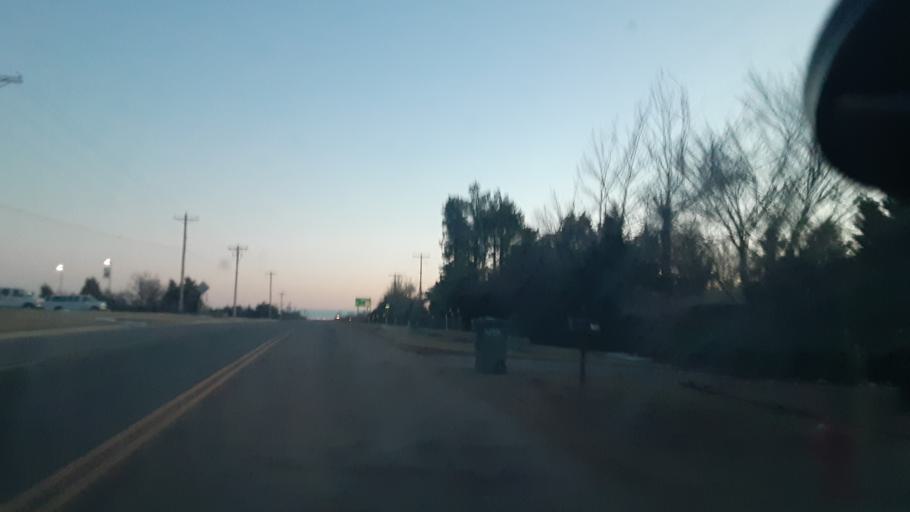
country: US
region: Oklahoma
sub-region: Oklahoma County
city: Edmond
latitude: 35.6637
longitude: -97.4250
